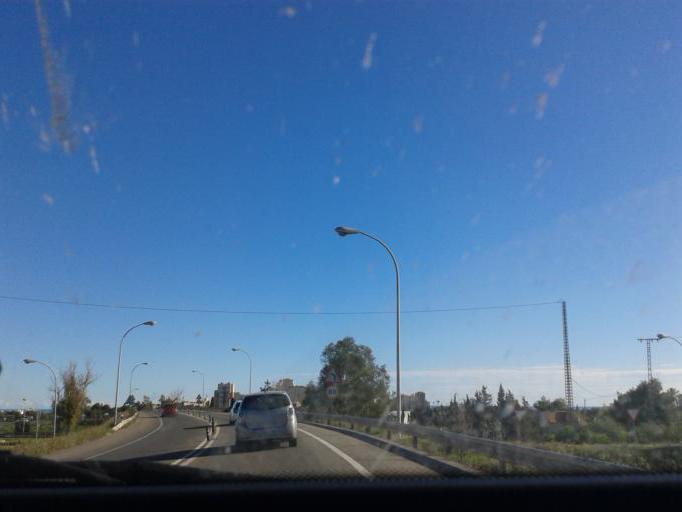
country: ES
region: Valencia
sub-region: Provincia de Alicante
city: San Juan de Alicante
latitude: 38.4145
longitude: -0.4217
